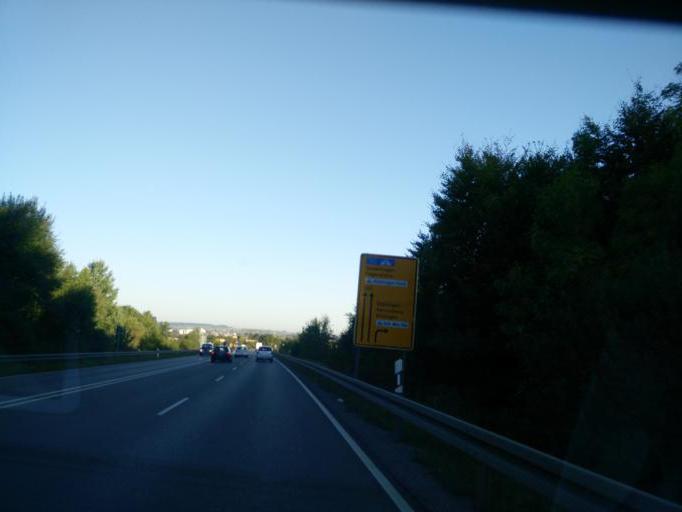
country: DE
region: Baden-Wuerttemberg
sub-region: Regierungsbezirk Stuttgart
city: Boeblingen
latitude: 48.6704
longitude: 8.9828
